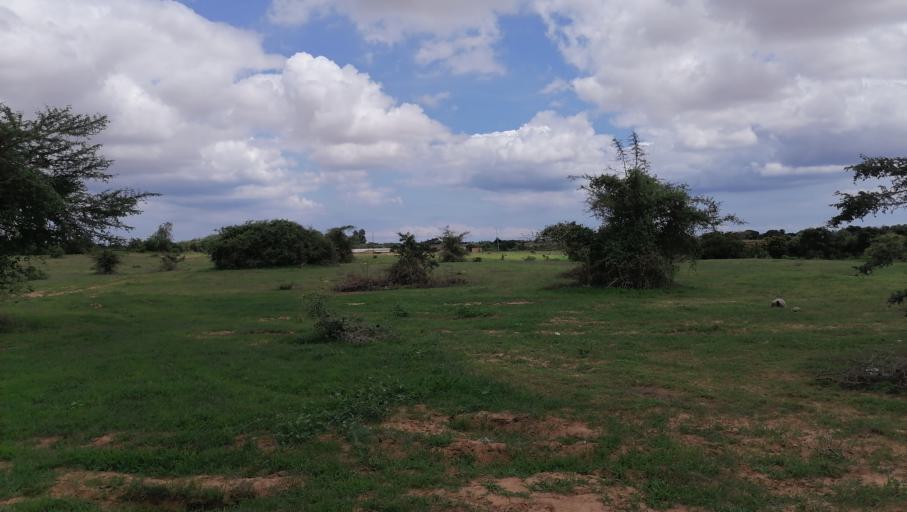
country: SN
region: Thies
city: Thies
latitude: 14.8232
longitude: -17.1451
